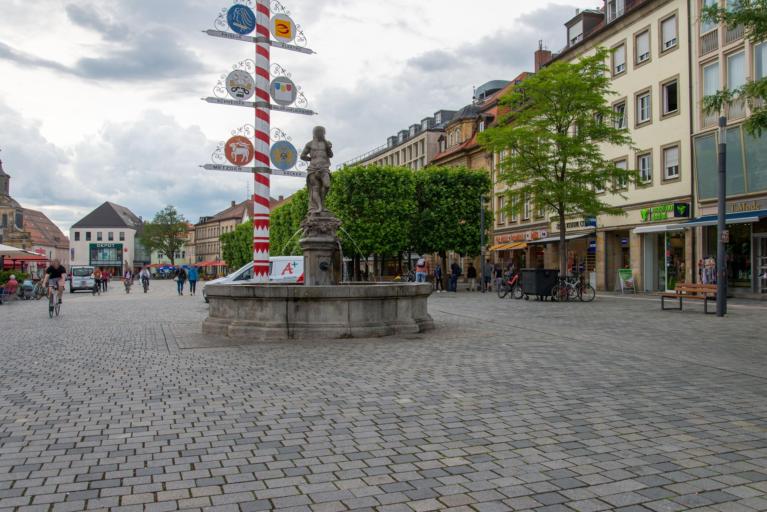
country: DE
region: Bavaria
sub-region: Upper Franconia
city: Bayreuth
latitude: 49.9445
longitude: 11.5747
